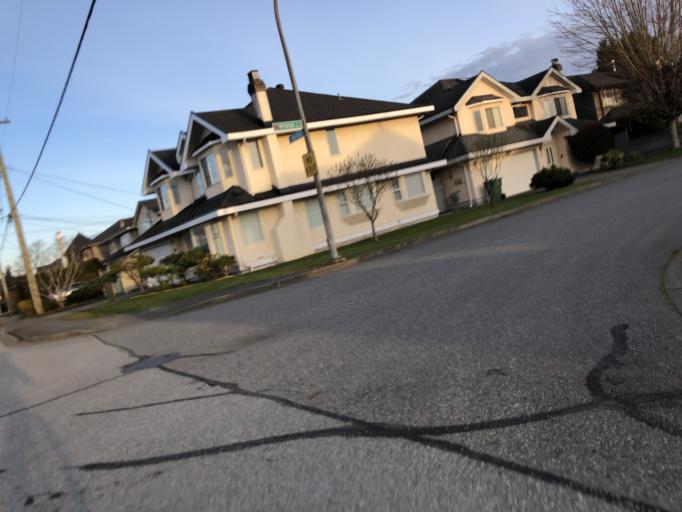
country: CA
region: British Columbia
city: Richmond
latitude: 49.1518
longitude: -123.1238
